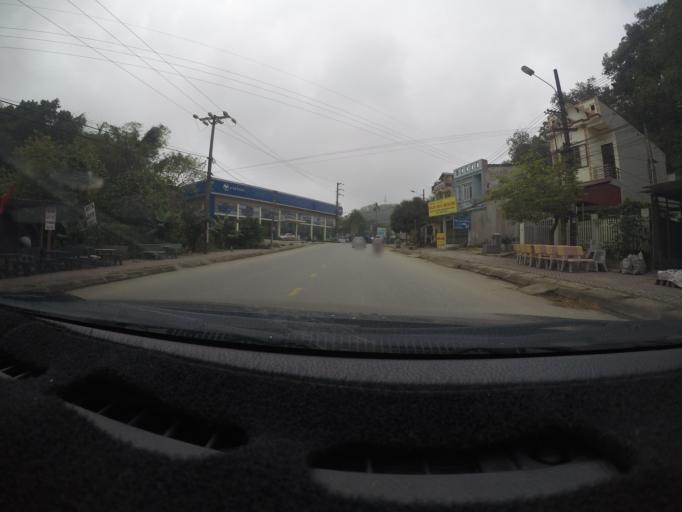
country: VN
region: Yen Bai
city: Yen Bai
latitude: 21.7334
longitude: 104.9521
